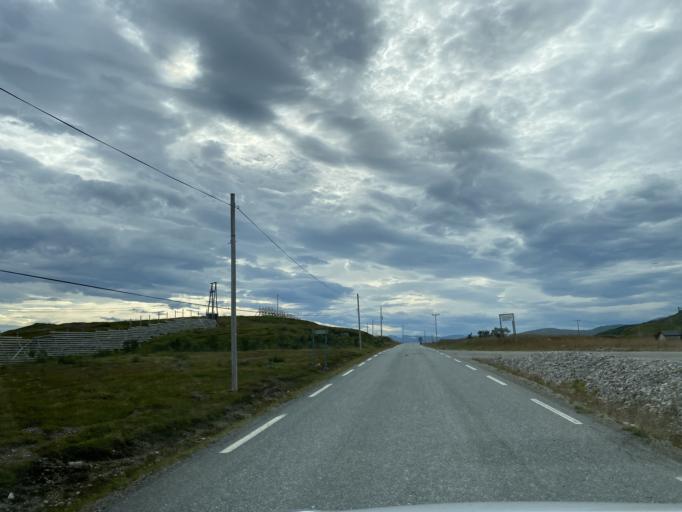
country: NO
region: Troms
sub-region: Karlsoy
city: Hansnes
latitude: 70.1001
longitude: 20.1056
